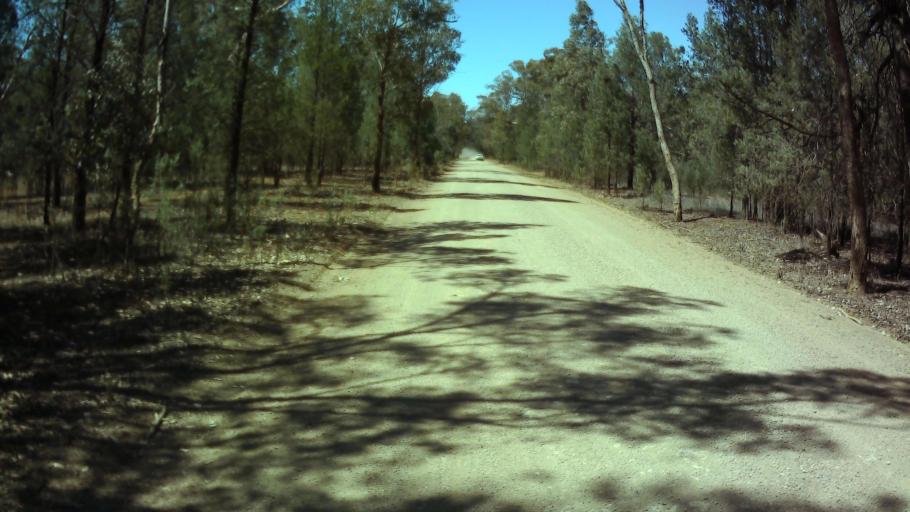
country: AU
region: New South Wales
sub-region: Weddin
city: Grenfell
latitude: -33.8551
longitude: 148.0875
